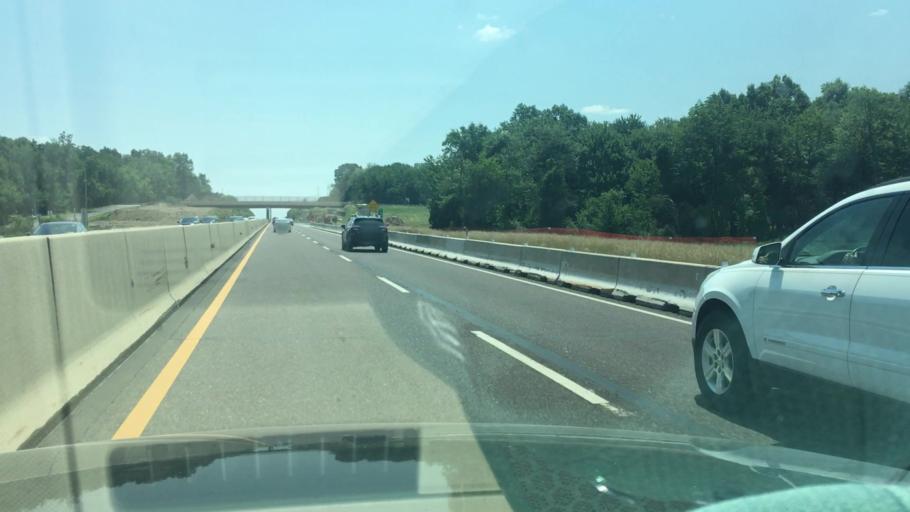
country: US
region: Pennsylvania
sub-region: Montgomery County
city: Woxall
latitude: 40.3559
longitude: -75.3937
